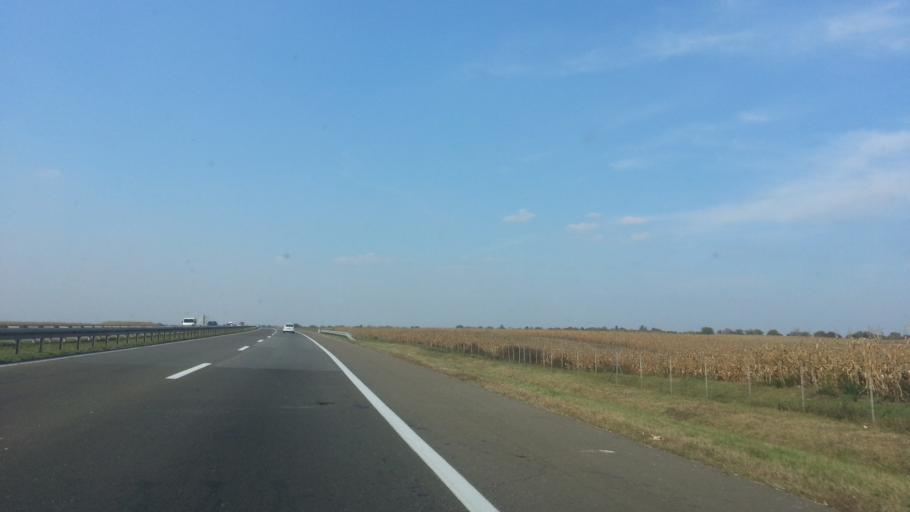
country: RS
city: Novi Banovci
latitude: 44.9226
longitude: 20.3036
